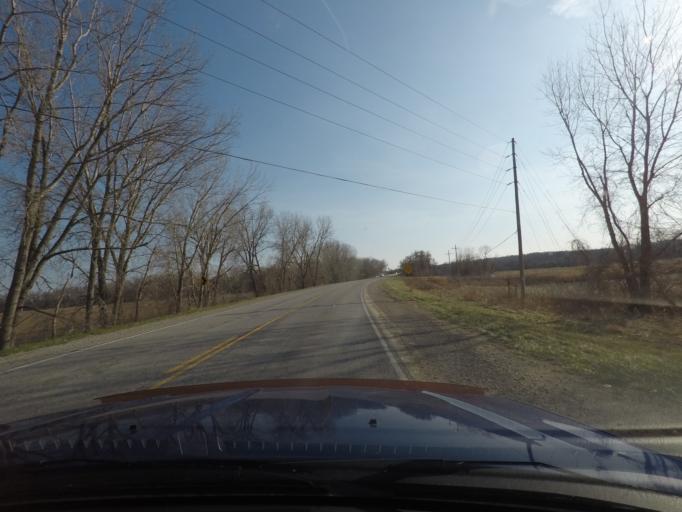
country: US
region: Kansas
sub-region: Douglas County
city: Lawrence
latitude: 39.0537
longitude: -95.3847
